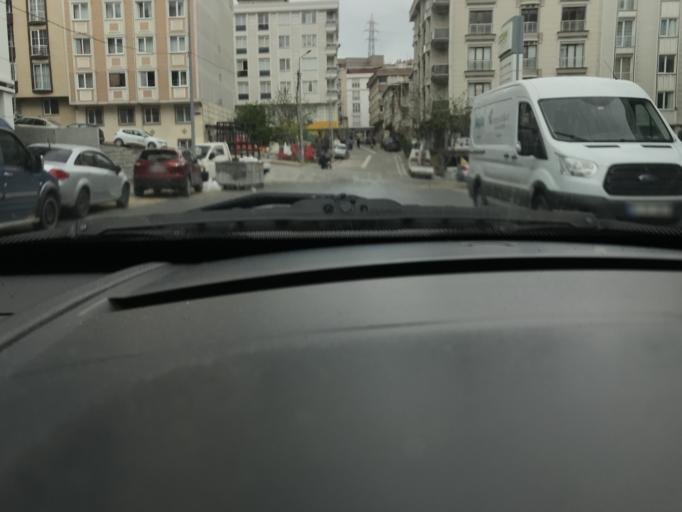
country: TR
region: Istanbul
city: Yakuplu
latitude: 41.0062
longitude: 28.6880
